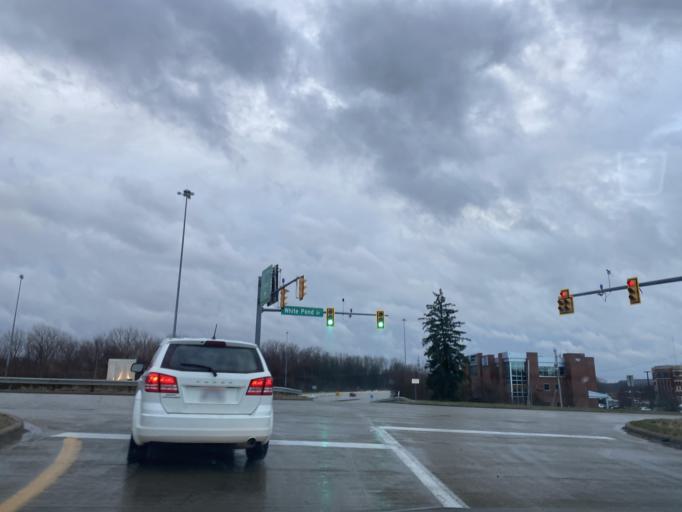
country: IN
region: Maharashtra
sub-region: Pune Division
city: Baramati
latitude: 18.1757
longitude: 74.4023
